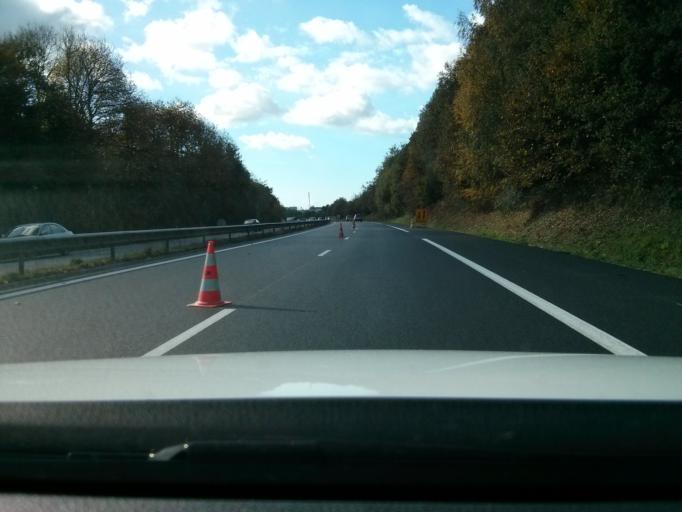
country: FR
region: Brittany
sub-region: Departement des Cotes-d'Armor
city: Plouer-sur-Rance
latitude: 48.5277
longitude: -2.0325
